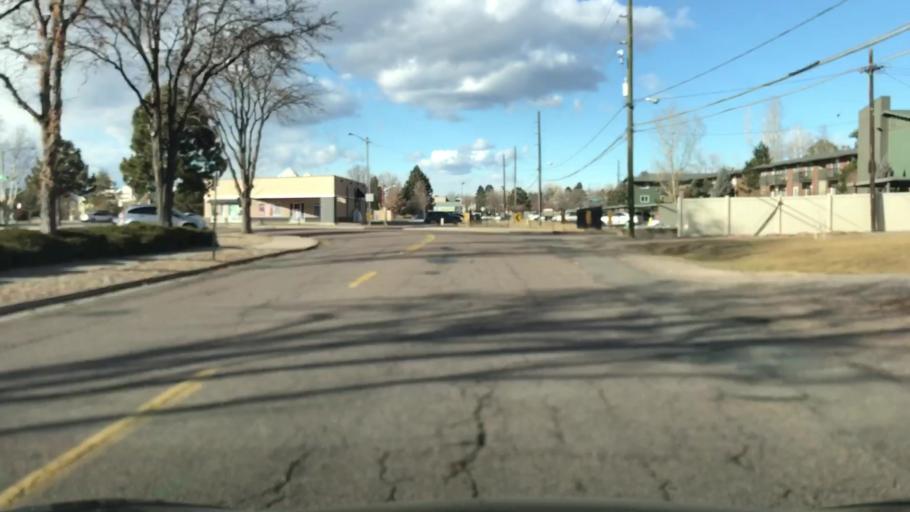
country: US
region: Colorado
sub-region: Arapahoe County
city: Glendale
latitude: 39.6952
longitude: -104.9022
